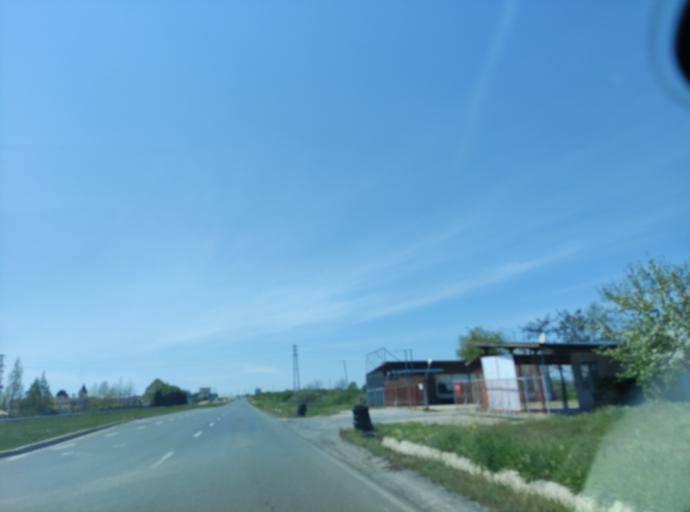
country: BG
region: Burgas
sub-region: Obshtina Nesebur
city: Ravda
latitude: 42.6585
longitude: 27.6863
